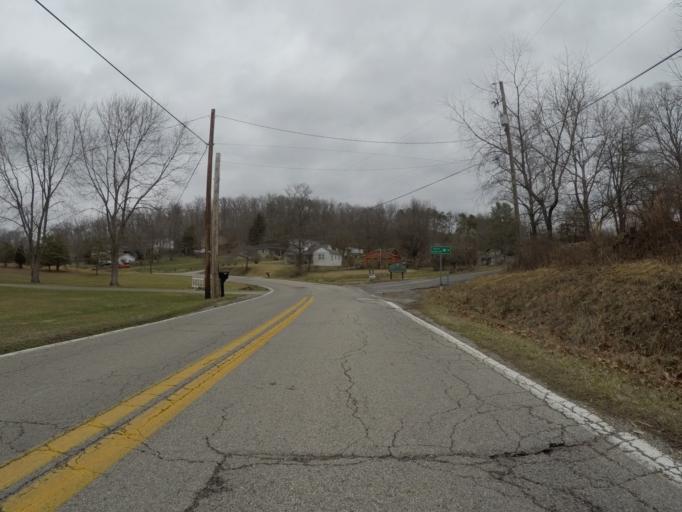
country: US
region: West Virginia
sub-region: Cabell County
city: Barboursville
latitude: 38.4363
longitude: -82.2433
